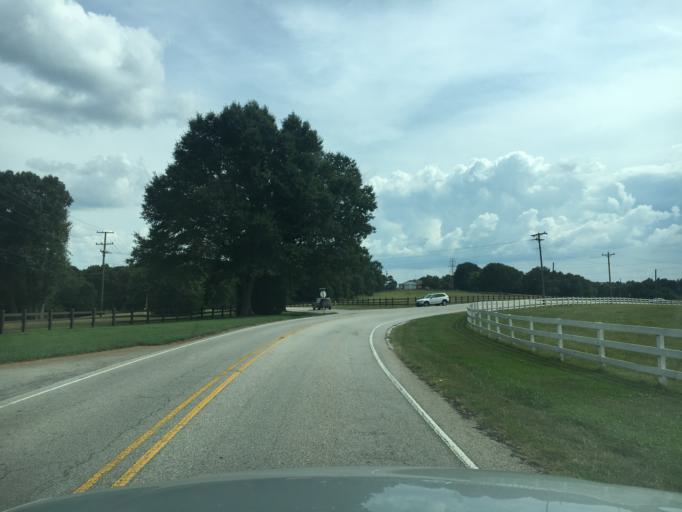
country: US
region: South Carolina
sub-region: Greenville County
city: Greer
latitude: 34.8771
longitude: -82.2403
